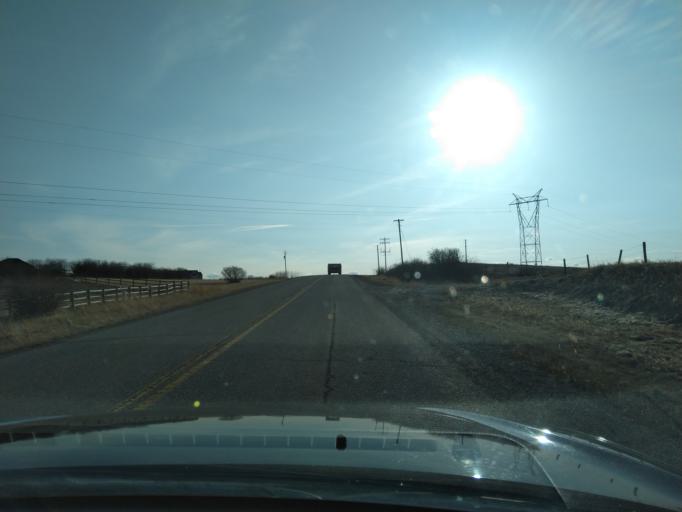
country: CA
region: Alberta
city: Cochrane
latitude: 51.1683
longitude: -114.4811
